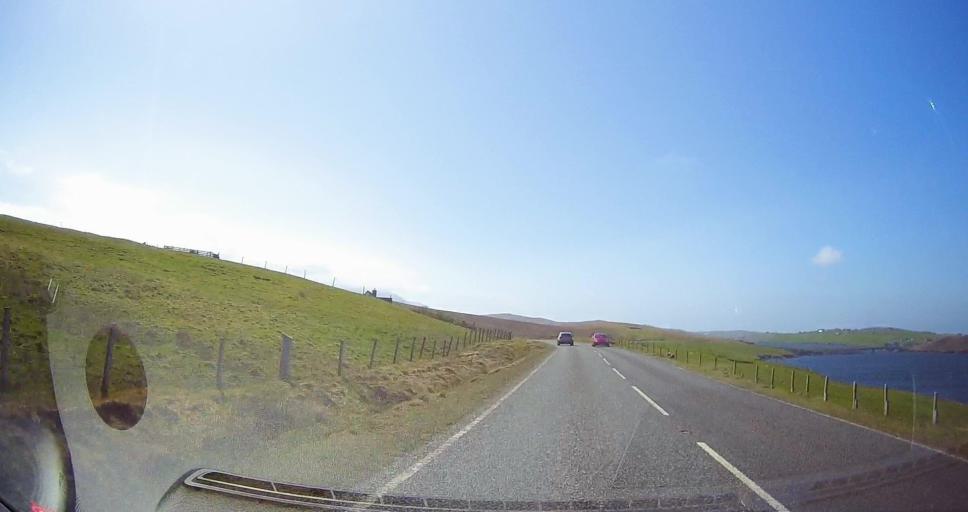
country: GB
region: Scotland
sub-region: Shetland Islands
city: Sandwick
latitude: 60.1124
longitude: -1.2955
